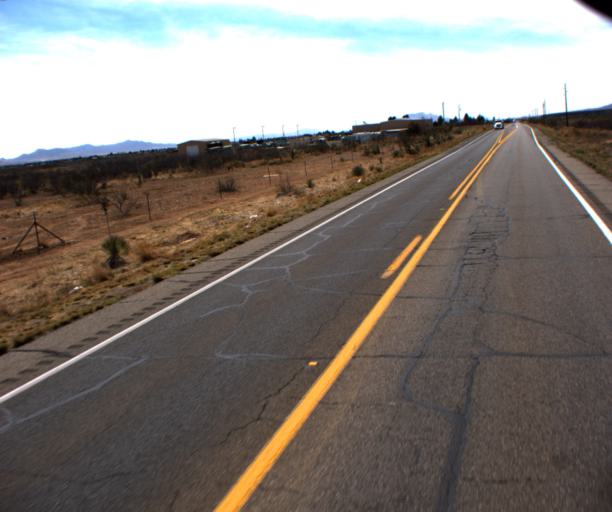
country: US
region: Arizona
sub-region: Cochise County
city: Pirtleville
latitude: 31.3745
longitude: -109.5794
